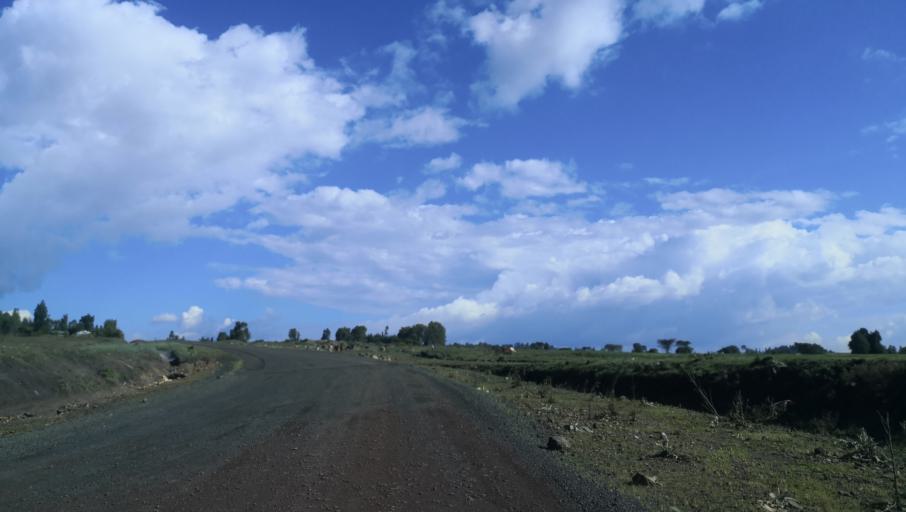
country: ET
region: Oromiya
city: Tulu Bolo
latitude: 8.5774
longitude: 38.2408
